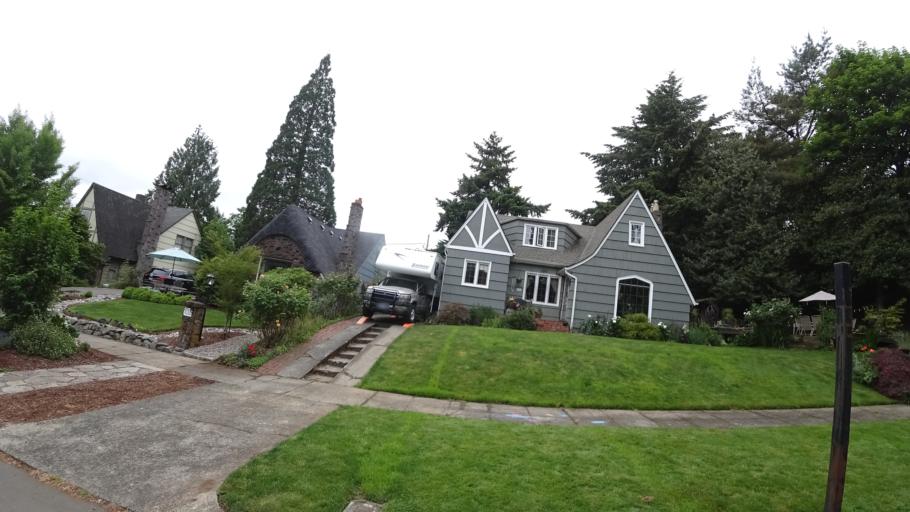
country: US
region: Oregon
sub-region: Multnomah County
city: Lents
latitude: 45.5396
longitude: -122.5995
